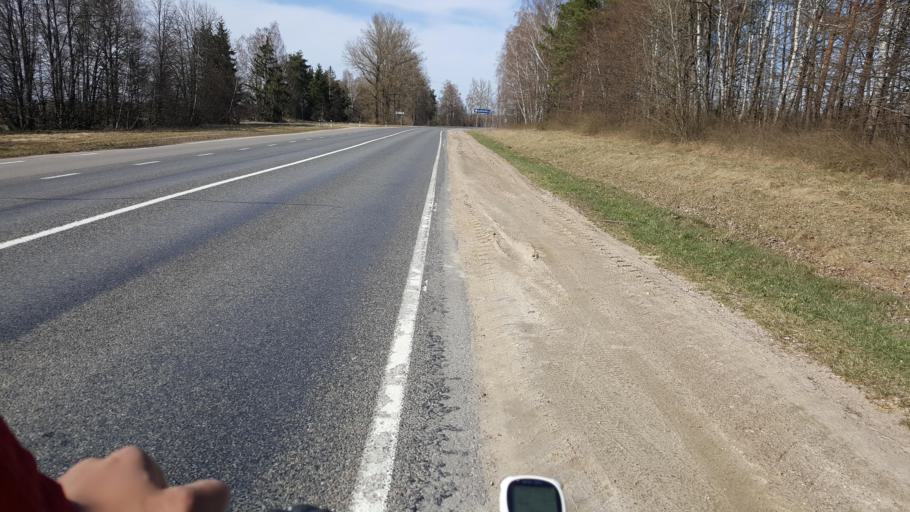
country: BY
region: Brest
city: Kamyanyets
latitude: 52.3539
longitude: 23.7763
